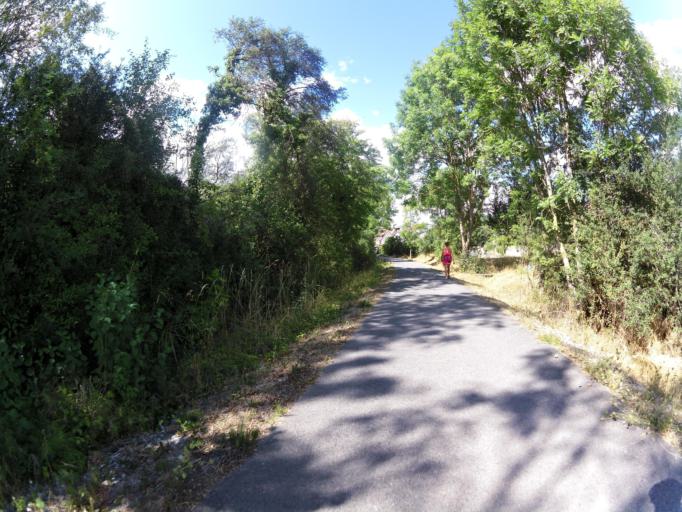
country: DE
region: Bavaria
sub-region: Regierungsbezirk Unterfranken
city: Gaukonigshofen
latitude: 49.6281
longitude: 10.0079
